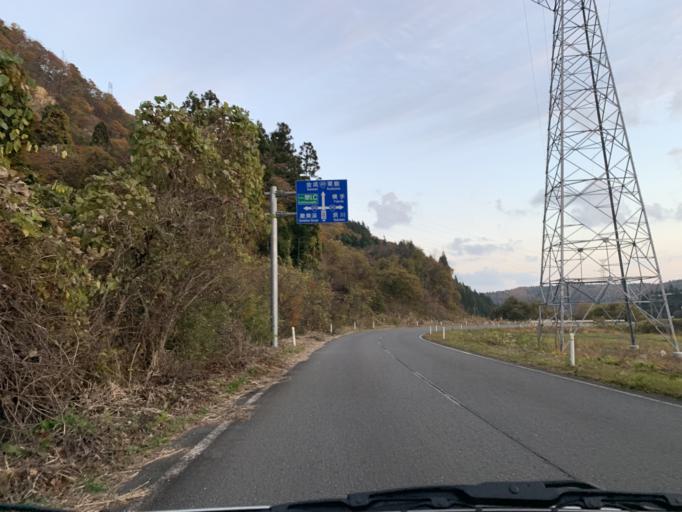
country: JP
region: Iwate
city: Ichinoseki
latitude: 38.9565
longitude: 141.0193
